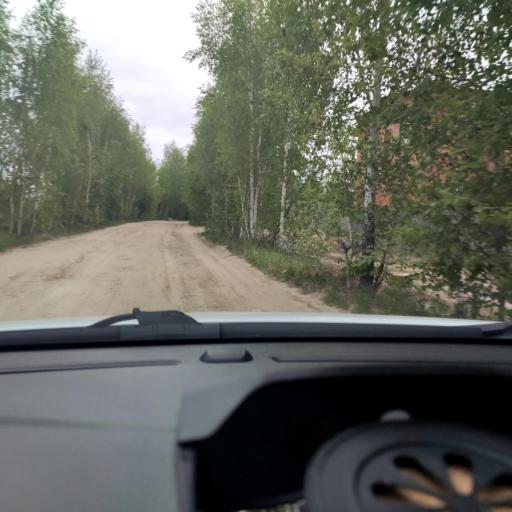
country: RU
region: Tatarstan
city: Vysokaya Gora
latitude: 55.8542
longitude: 49.2506
